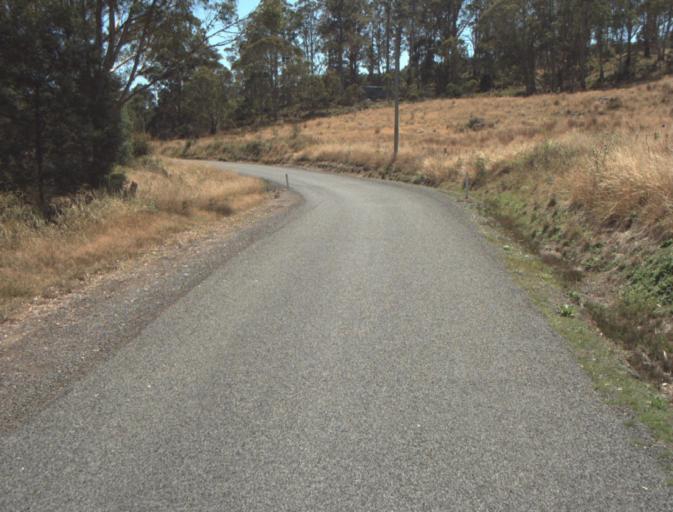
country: AU
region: Tasmania
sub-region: Launceston
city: Newstead
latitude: -41.3586
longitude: 147.3026
